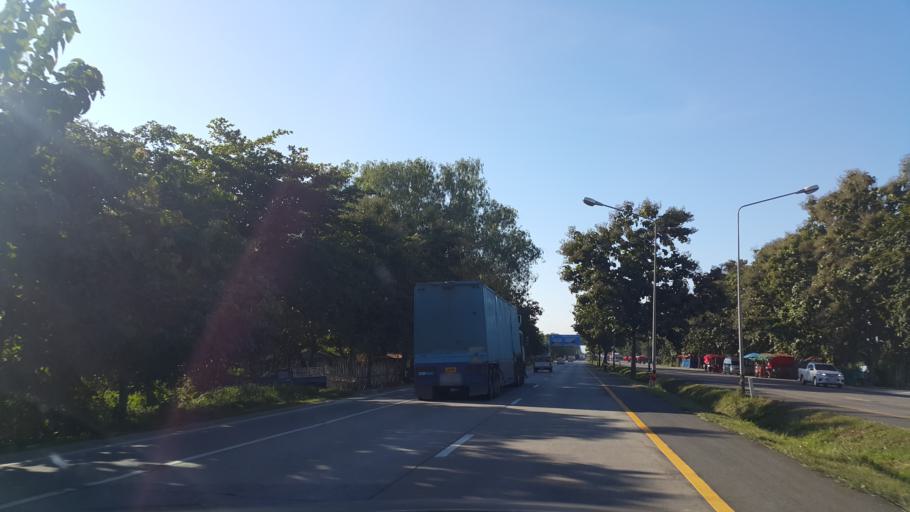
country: TH
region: Lamphun
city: Lamphun
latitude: 18.5436
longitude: 99.0622
